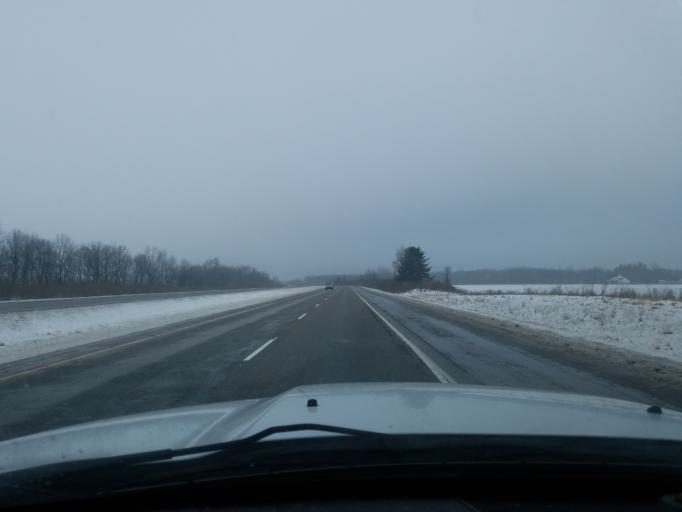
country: US
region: Indiana
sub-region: Fulton County
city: Rochester
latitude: 41.0038
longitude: -86.1676
